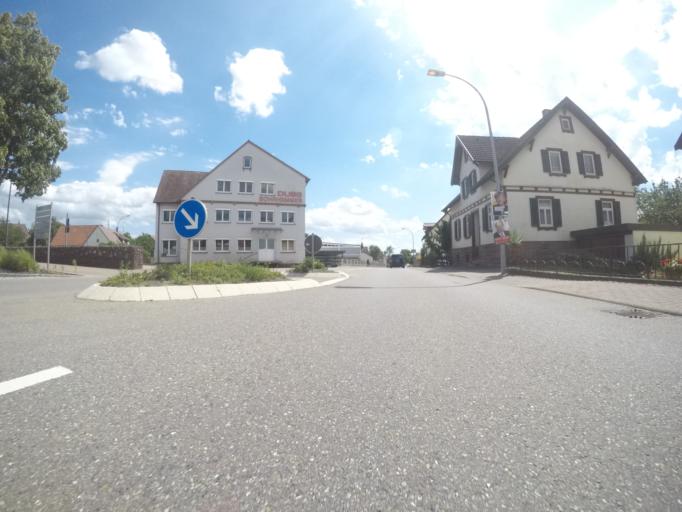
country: DE
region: Baden-Wuerttemberg
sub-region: Karlsruhe Region
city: Neubulach
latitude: 48.6629
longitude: 8.6915
